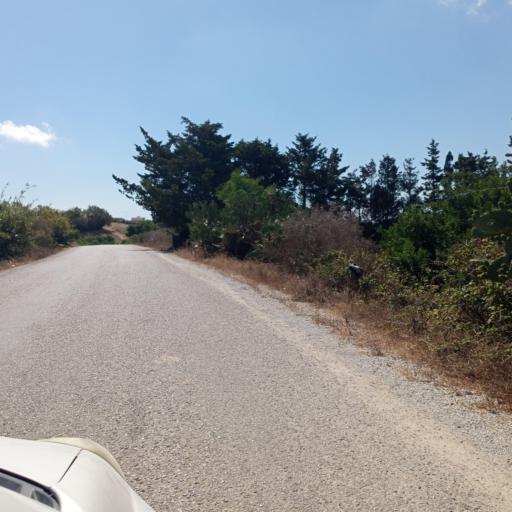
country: TN
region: Nabul
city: Qulaybiyah
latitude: 36.8603
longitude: 11.0437
